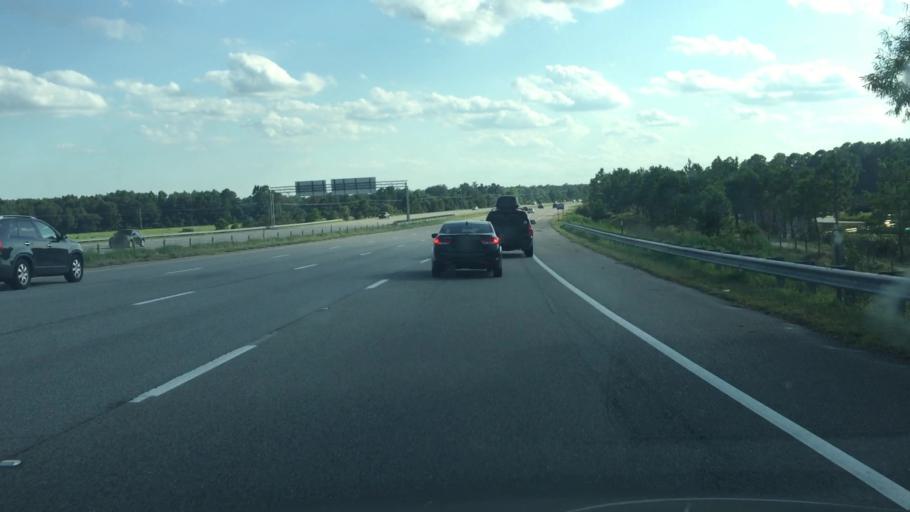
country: US
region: South Carolina
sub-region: Horry County
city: North Myrtle Beach
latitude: 33.8415
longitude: -78.7034
